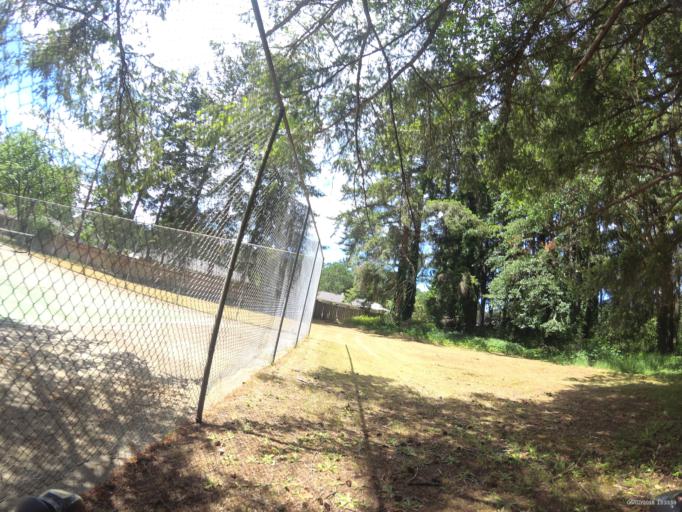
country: US
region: Washington
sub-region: Pierce County
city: University Place
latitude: 47.2069
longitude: -122.5621
